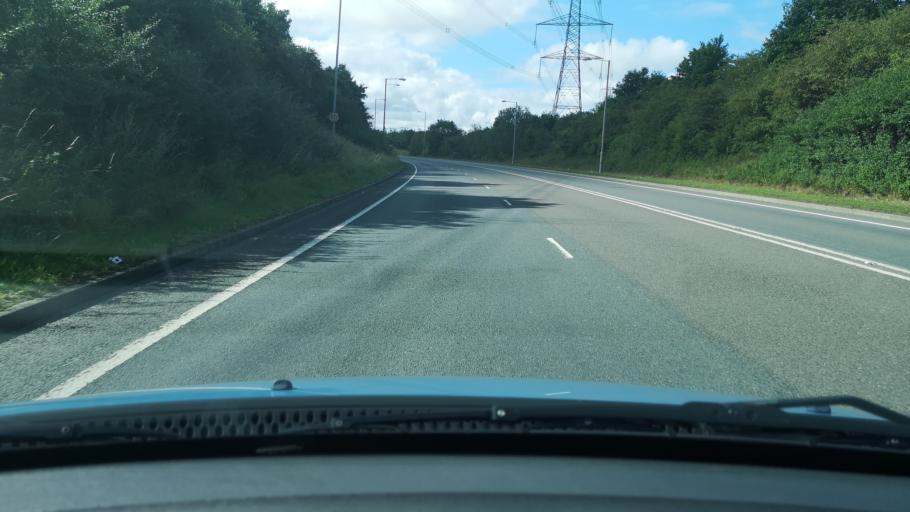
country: GB
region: England
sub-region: City and Borough of Wakefield
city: Normanton
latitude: 53.6881
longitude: -1.4080
